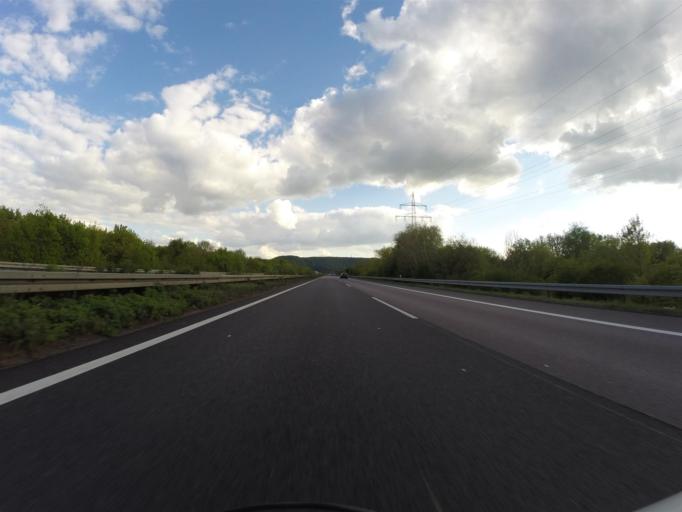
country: DE
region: Saarland
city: Rehlingen-Siersburg
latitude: 49.3740
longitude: 6.6964
